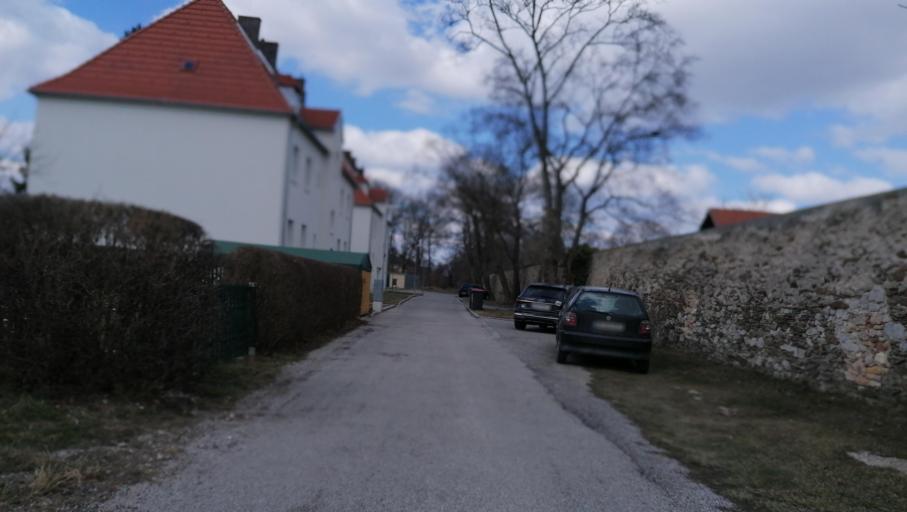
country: AT
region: Lower Austria
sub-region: Wiener Neustadt Stadt
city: Wiener Neustadt
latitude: 47.7951
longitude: 16.2458
